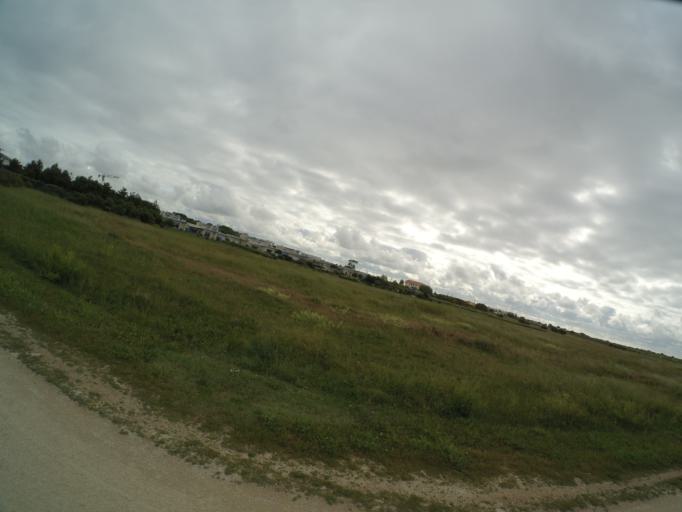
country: FR
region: Poitou-Charentes
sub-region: Departement de la Charente-Maritime
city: La Rochelle
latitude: 46.1349
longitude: -1.1514
